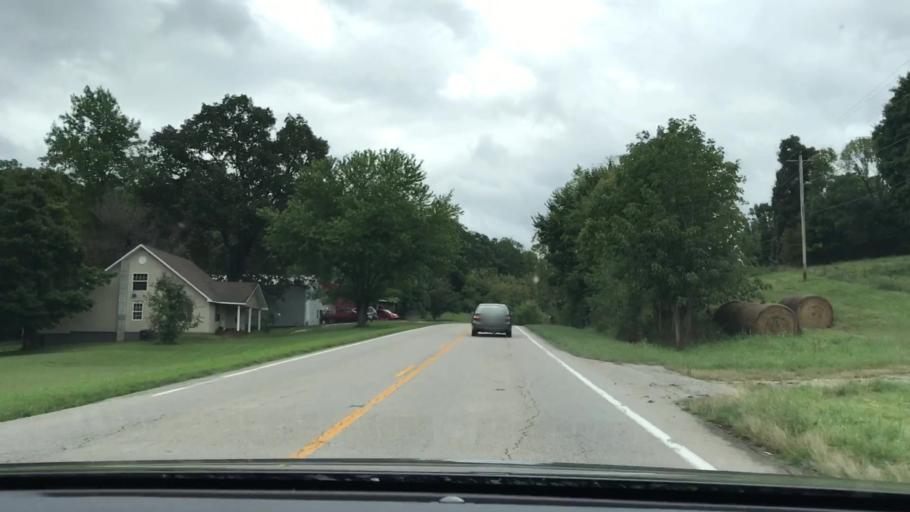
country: US
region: Kentucky
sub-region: Metcalfe County
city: Edmonton
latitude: 36.9058
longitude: -85.7568
